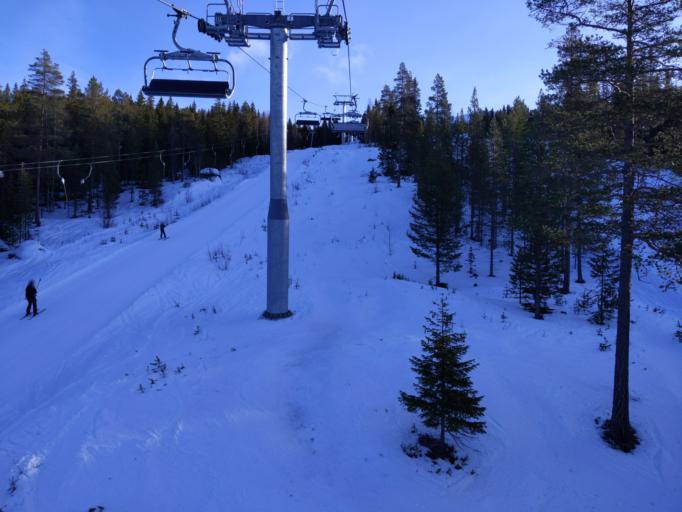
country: SE
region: Jaemtland
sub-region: Harjedalens Kommun
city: Sveg
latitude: 62.4125
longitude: 13.9579
